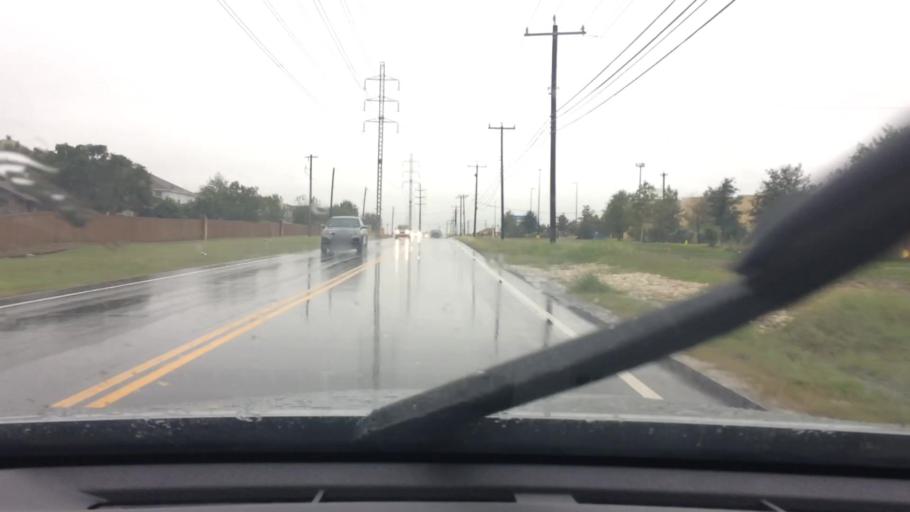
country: US
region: Texas
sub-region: Bexar County
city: Kirby
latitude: 29.4653
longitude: -98.3546
